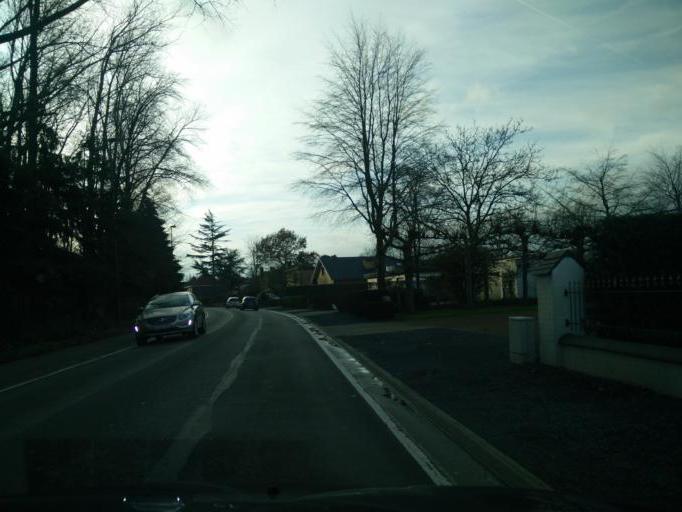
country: BE
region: Flanders
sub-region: Provincie Oost-Vlaanderen
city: Merelbeke
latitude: 50.9965
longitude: 3.7390
